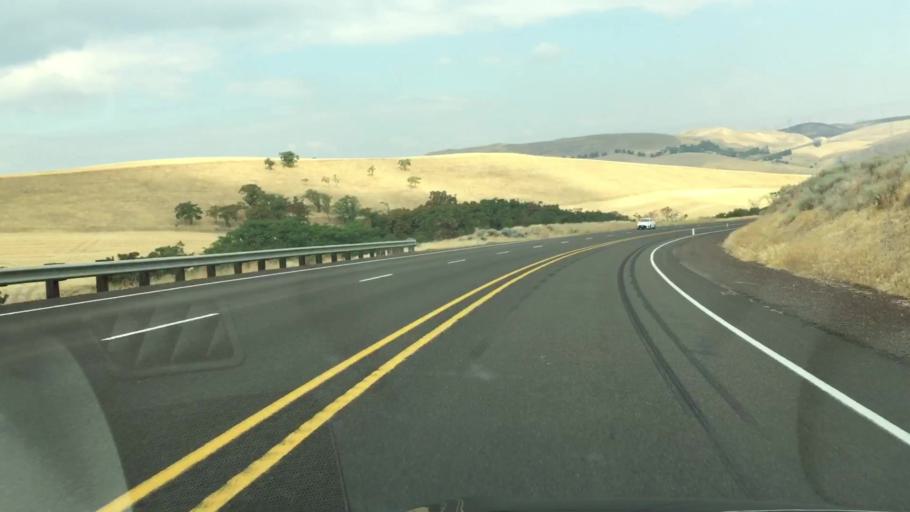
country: US
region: Oregon
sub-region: Wasco County
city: The Dalles
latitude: 45.5523
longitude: -121.1004
